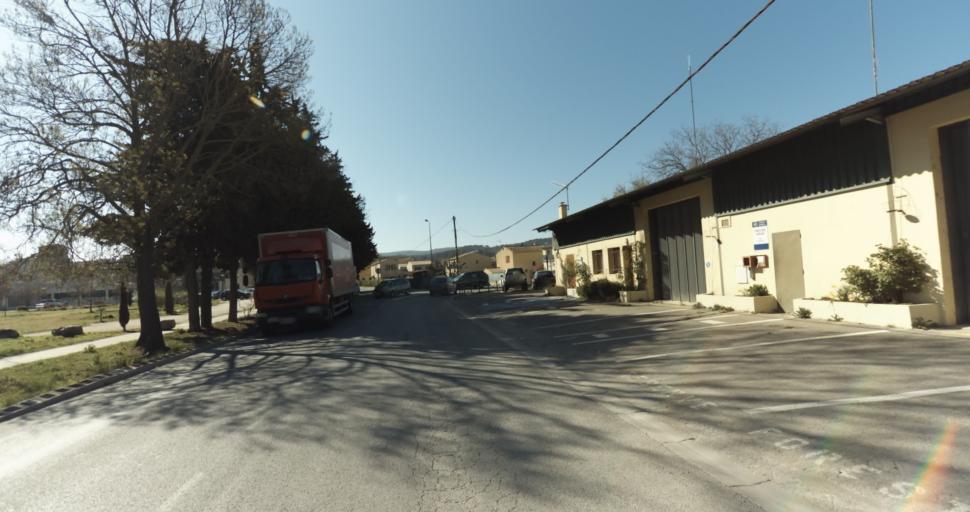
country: FR
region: Provence-Alpes-Cote d'Azur
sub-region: Departement des Bouches-du-Rhone
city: Peyrolles-en-Provence
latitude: 43.6494
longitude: 5.5809
